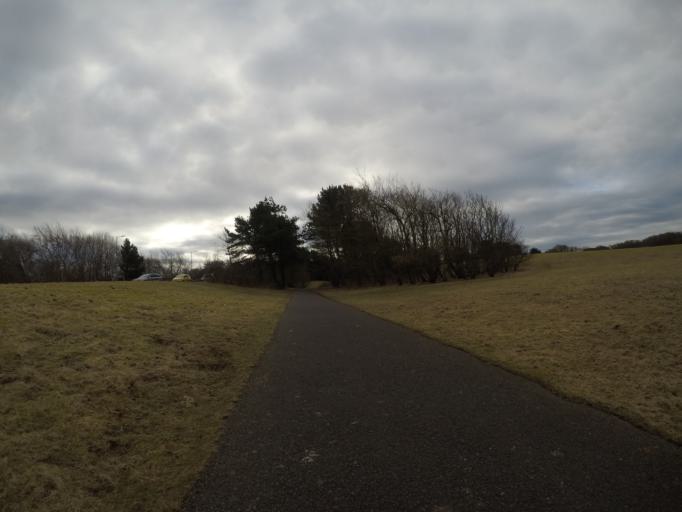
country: GB
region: Scotland
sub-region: North Ayrshire
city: Irvine
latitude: 55.6056
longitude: -4.6812
